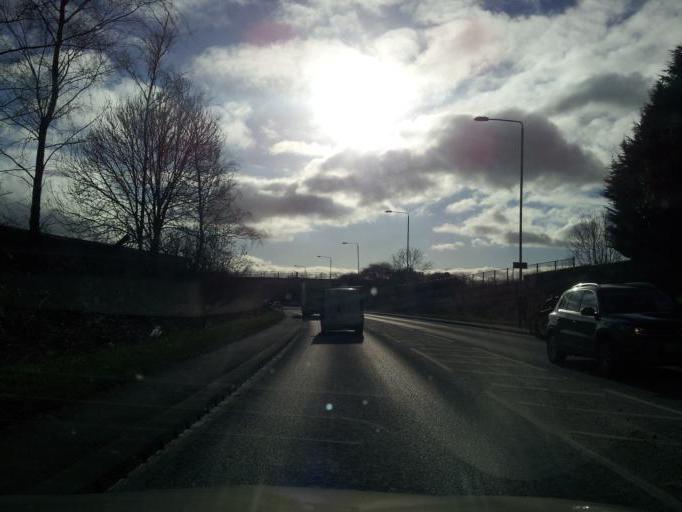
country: GB
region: England
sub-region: Nottinghamshire
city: Sutton in Ashfield
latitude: 53.1183
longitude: -1.2543
